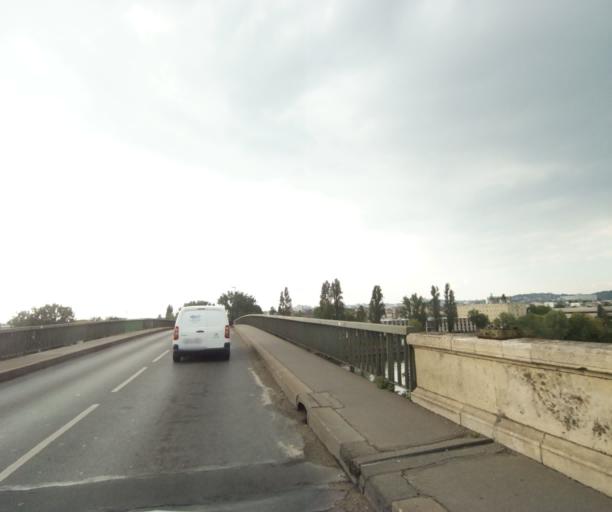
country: FR
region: Ile-de-France
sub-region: Departement des Hauts-de-Seine
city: Colombes
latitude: 48.9326
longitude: 2.2422
